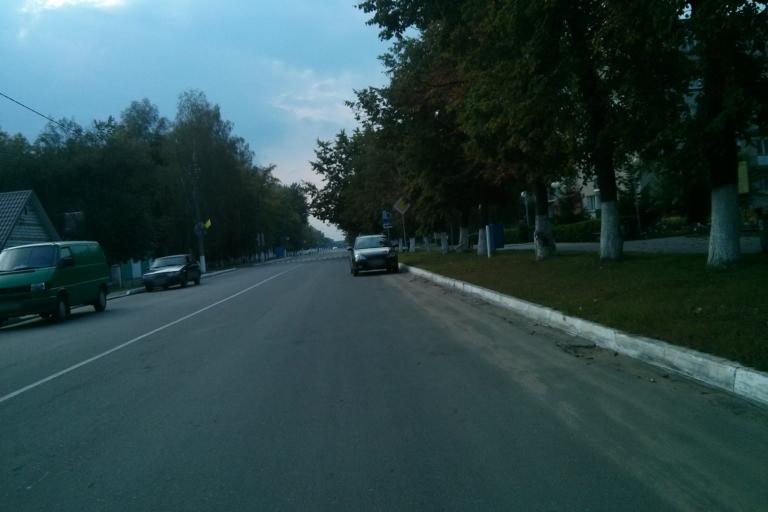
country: BY
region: Minsk
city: Chervyen'
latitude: 53.7179
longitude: 28.4047
